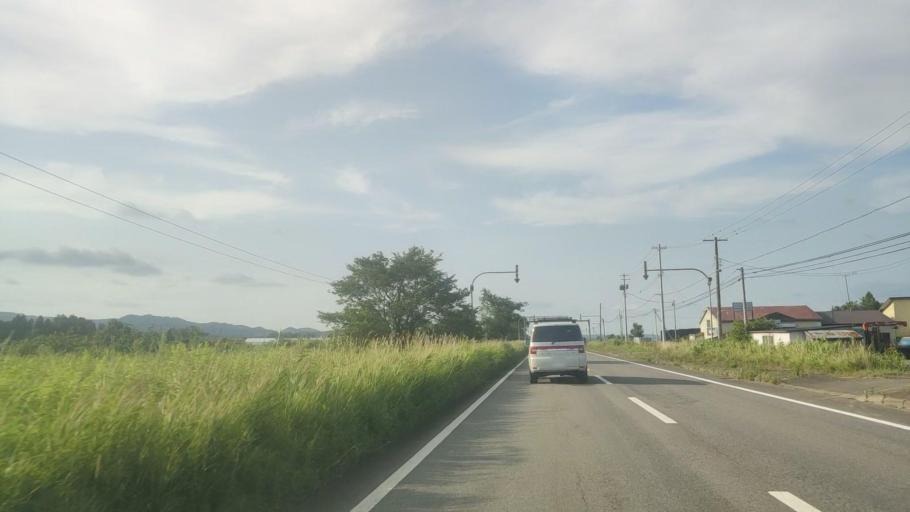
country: JP
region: Hokkaido
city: Chitose
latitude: 42.9582
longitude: 141.7983
